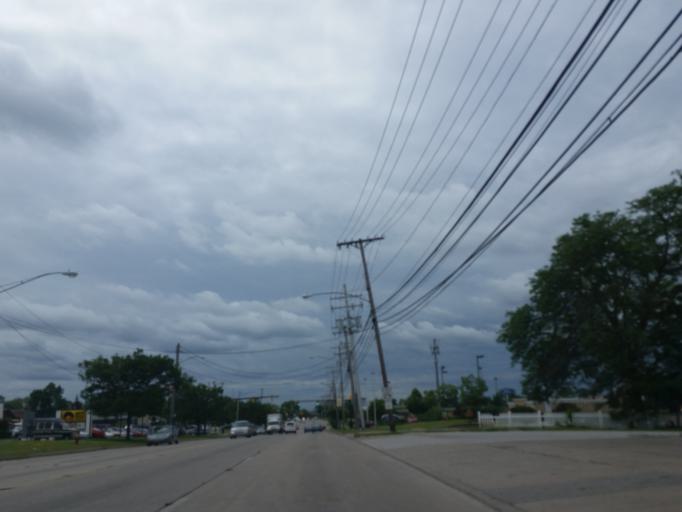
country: US
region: Ohio
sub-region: Cuyahoga County
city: Bedford Heights
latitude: 41.4156
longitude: -81.5374
